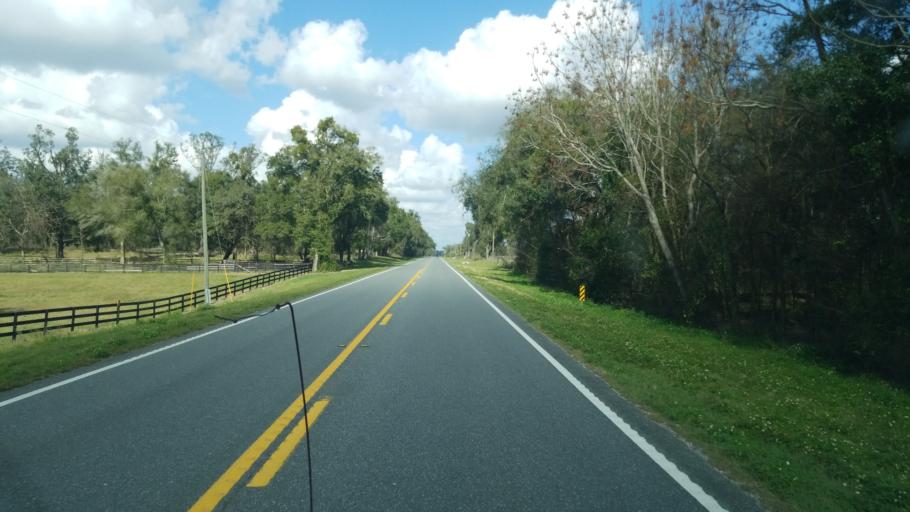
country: US
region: Florida
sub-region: Sumter County
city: Wildwood
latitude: 28.9080
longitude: -82.1200
